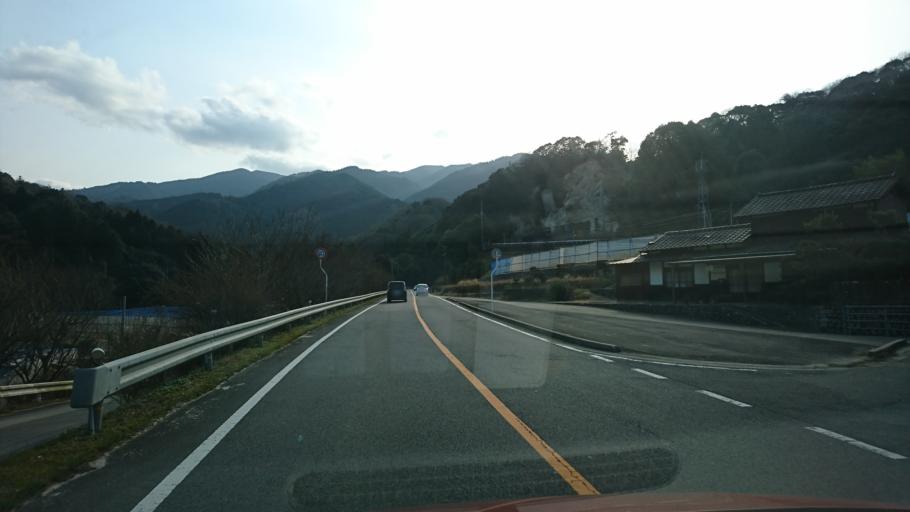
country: JP
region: Ehime
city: Hojo
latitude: 33.9755
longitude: 132.9037
